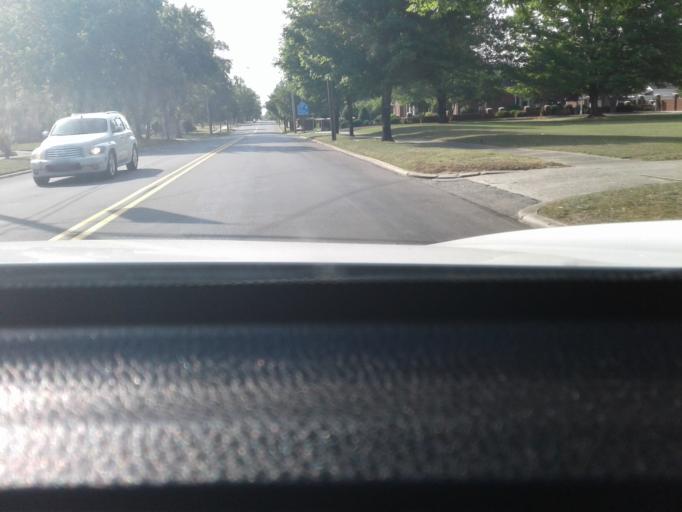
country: US
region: North Carolina
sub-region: Johnston County
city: Benson
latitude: 35.3860
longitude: -78.5560
